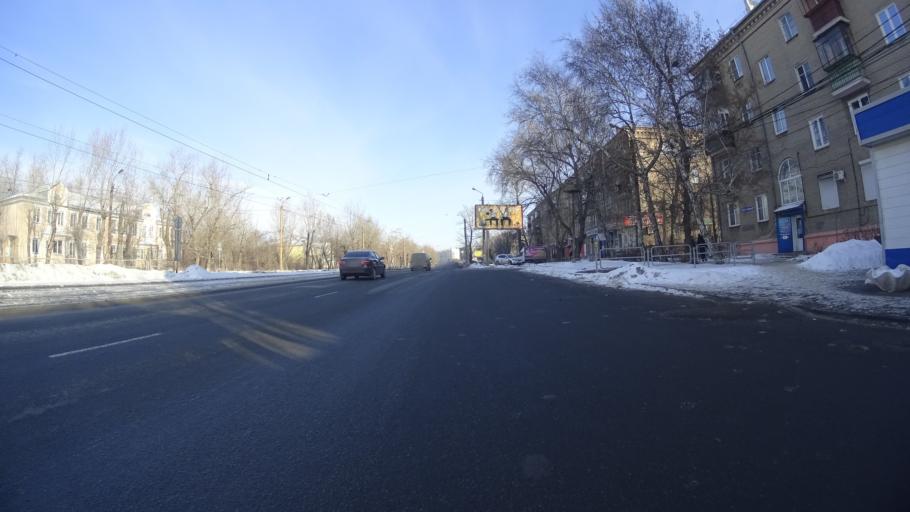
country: RU
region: Chelyabinsk
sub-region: Gorod Chelyabinsk
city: Chelyabinsk
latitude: 55.1855
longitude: 61.4250
